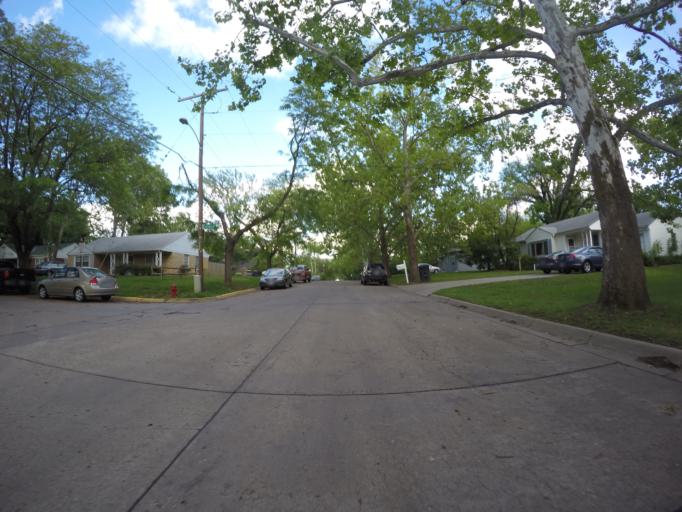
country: US
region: Kansas
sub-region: Riley County
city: Manhattan
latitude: 39.1944
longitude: -96.5912
